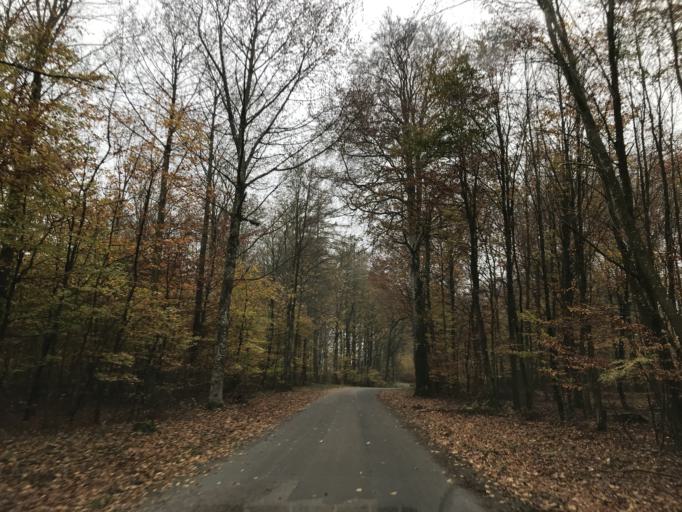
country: SE
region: Skane
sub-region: Klippans Kommun
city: Ljungbyhed
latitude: 55.9870
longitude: 13.2008
